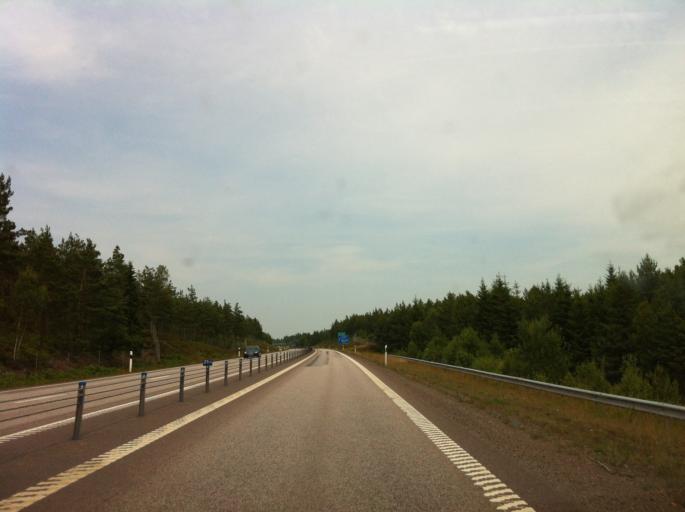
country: SE
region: Kalmar
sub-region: Torsas Kommun
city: Torsas
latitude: 56.4861
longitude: 16.0834
